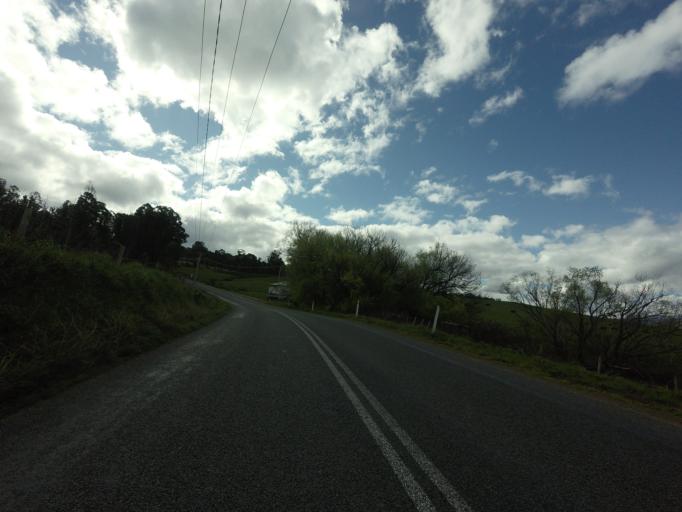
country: AU
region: Tasmania
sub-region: Huon Valley
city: Geeveston
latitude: -43.2028
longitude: 146.9651
